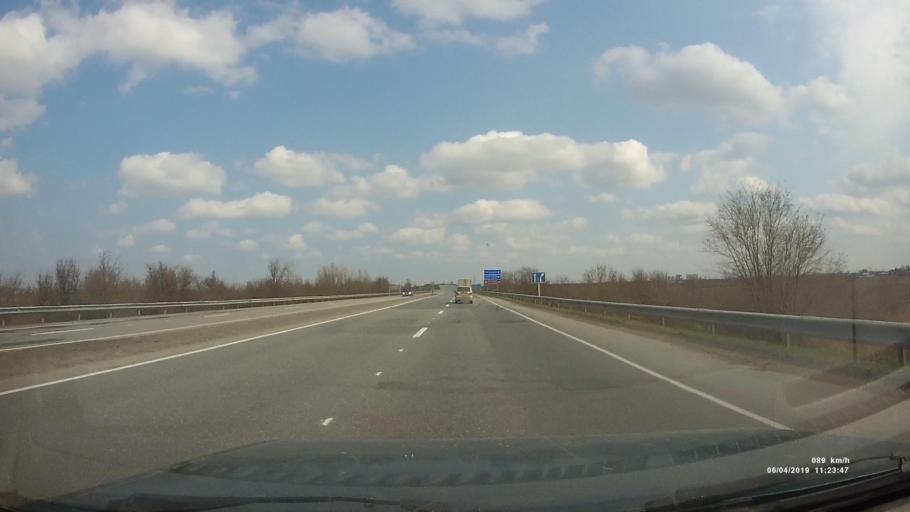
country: RU
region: Rostov
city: Bataysk
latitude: 47.1384
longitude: 39.6820
